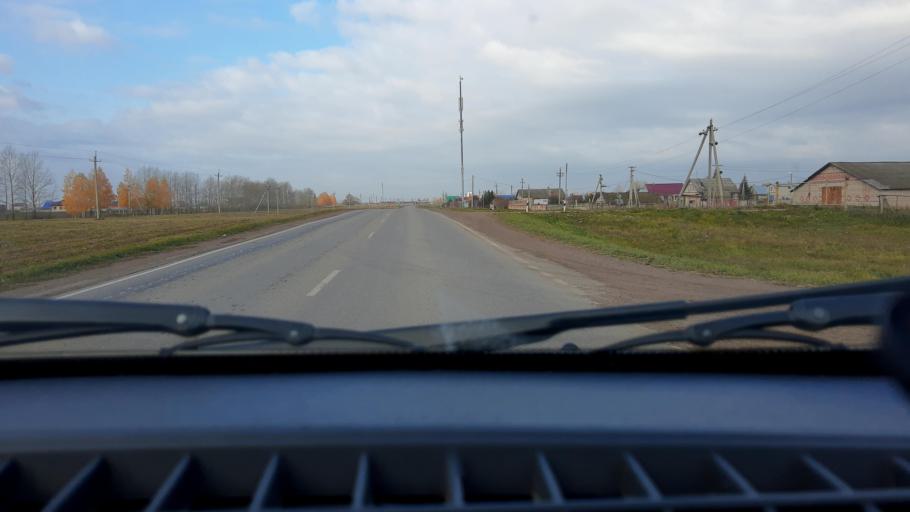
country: RU
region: Bashkortostan
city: Kabakovo
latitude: 54.5409
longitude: 56.1334
